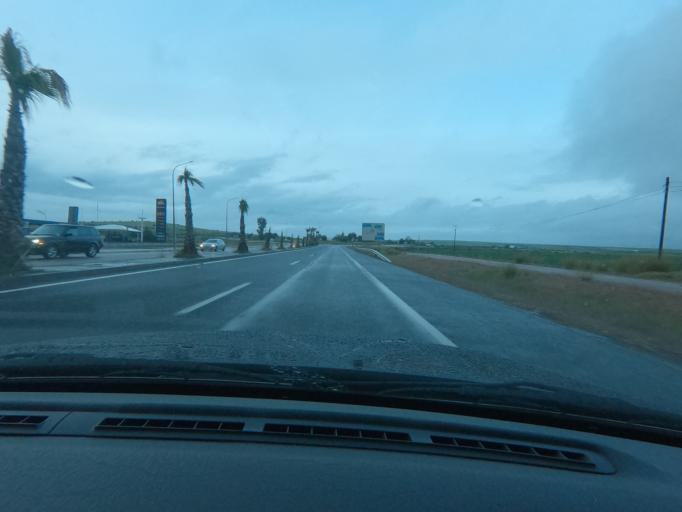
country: ES
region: Extremadura
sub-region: Provincia de Badajoz
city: Merida
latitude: 38.9385
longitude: -6.3439
